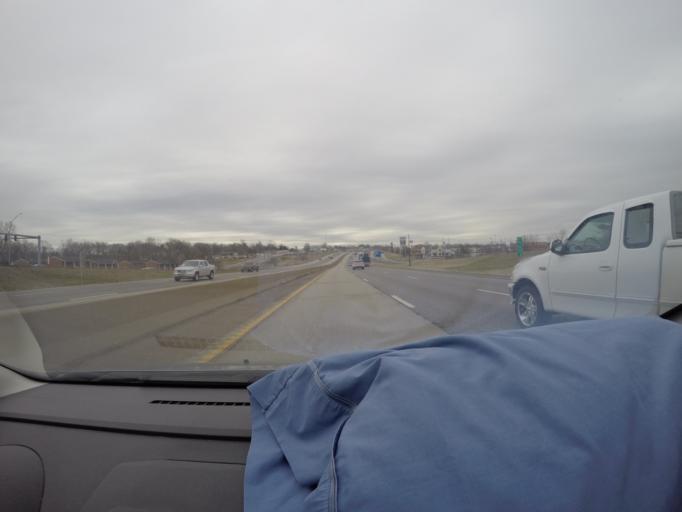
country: US
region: Missouri
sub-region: Saint Charles County
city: Saint Charles
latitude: 38.7862
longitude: -90.5309
